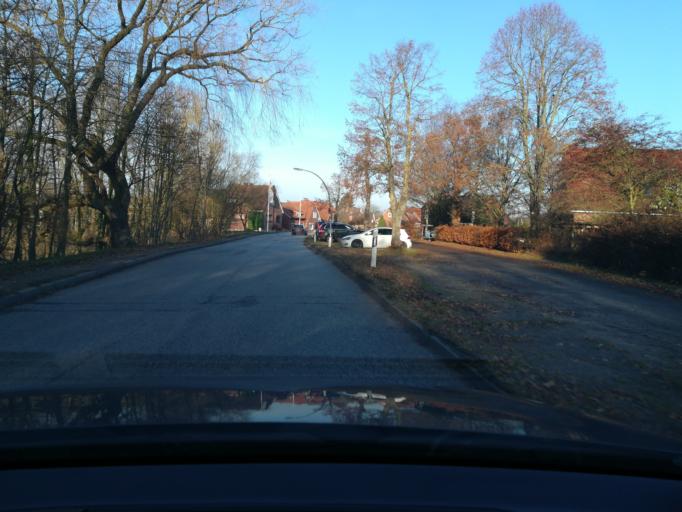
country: DE
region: Lower Saxony
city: Stelle
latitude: 53.4500
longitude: 10.1339
